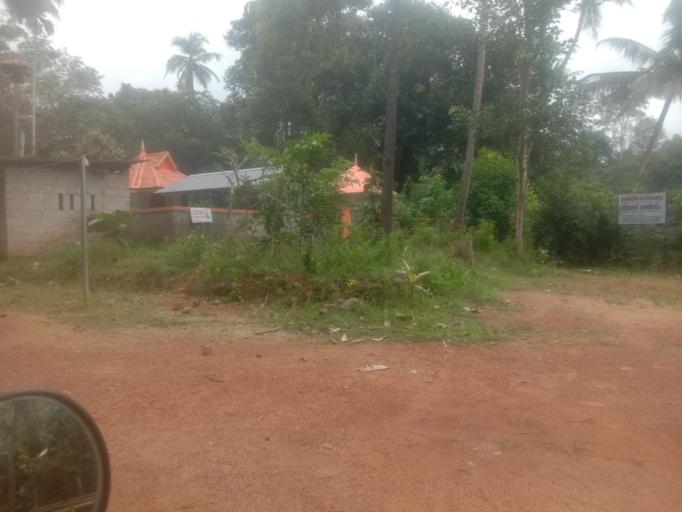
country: IN
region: Kerala
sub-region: Thiruvananthapuram
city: Nedumangad
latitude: 8.7011
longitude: 76.9575
